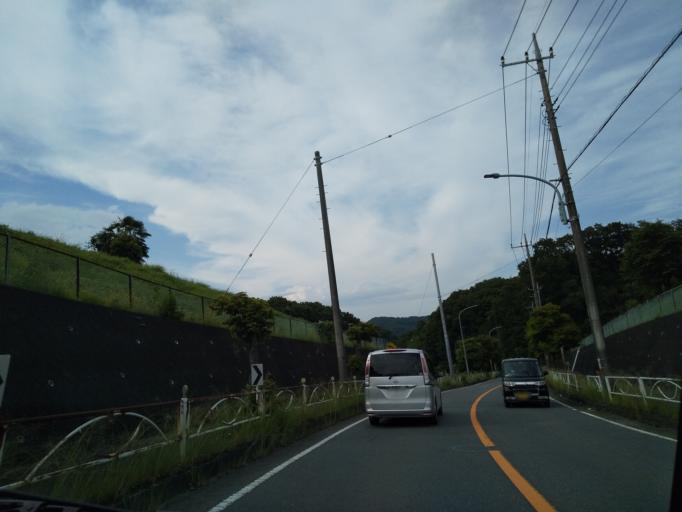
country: JP
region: Kanagawa
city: Atsugi
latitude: 35.4793
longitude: 139.3173
